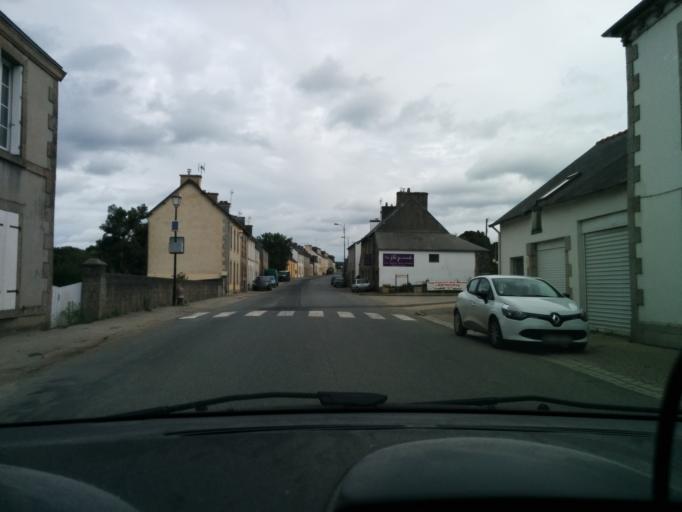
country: FR
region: Brittany
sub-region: Departement du Finistere
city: Brasparts
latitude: 48.3029
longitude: -3.9557
